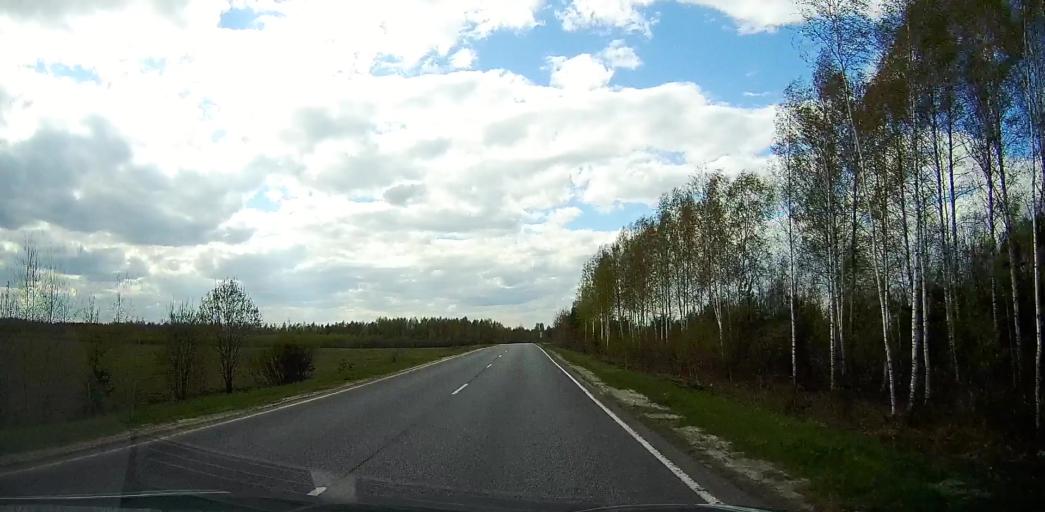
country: RU
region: Moskovskaya
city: Rakhmanovo
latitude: 55.6525
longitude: 38.6455
